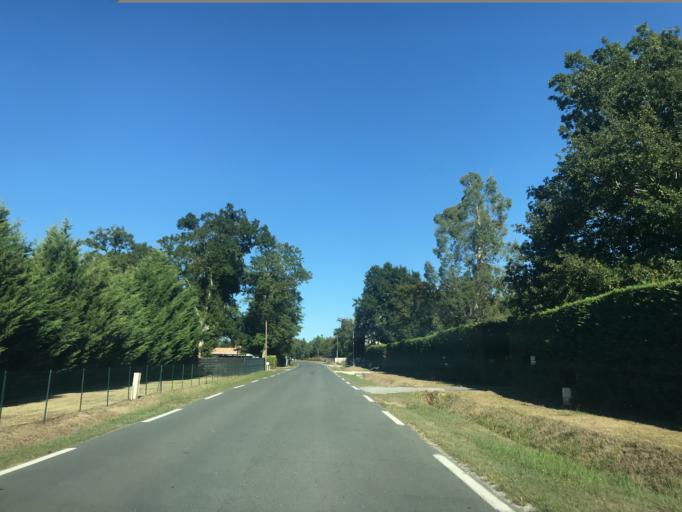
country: FR
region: Aquitaine
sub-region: Departement de la Gironde
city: Mios
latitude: 44.6348
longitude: -0.8914
